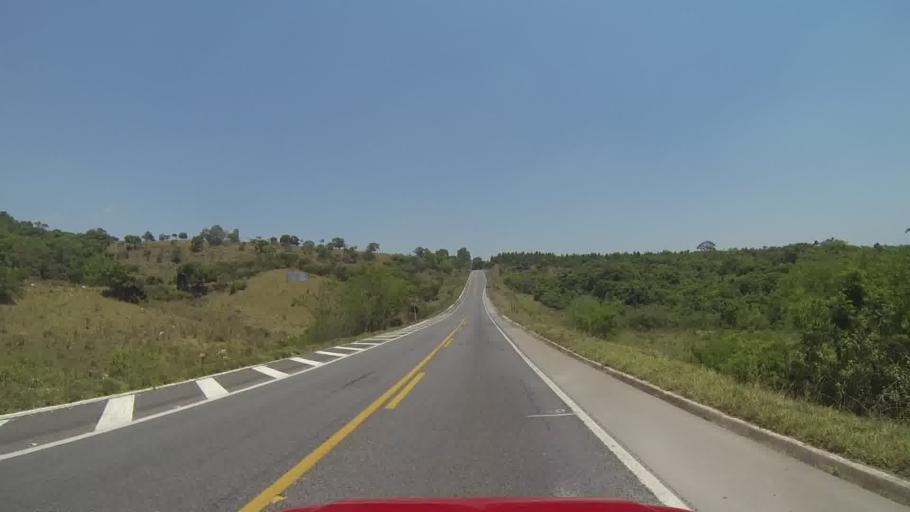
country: BR
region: Minas Gerais
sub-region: Itapecerica
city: Itapecerica
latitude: -20.2771
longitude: -45.1242
